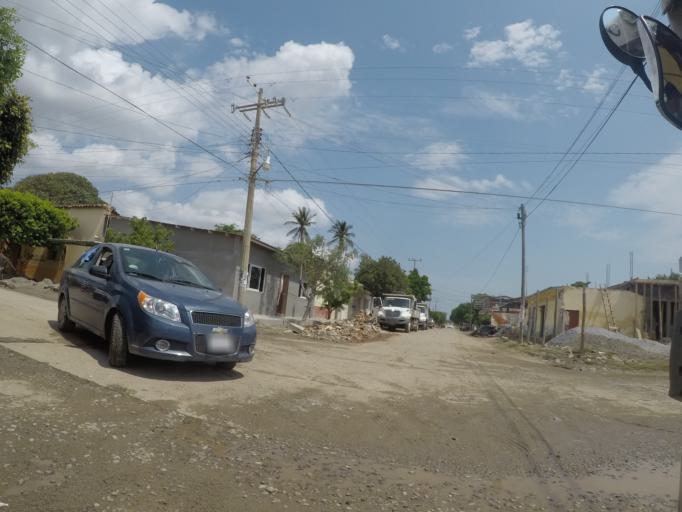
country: MX
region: Oaxaca
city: Union Hidalgo
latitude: 16.4717
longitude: -94.8282
